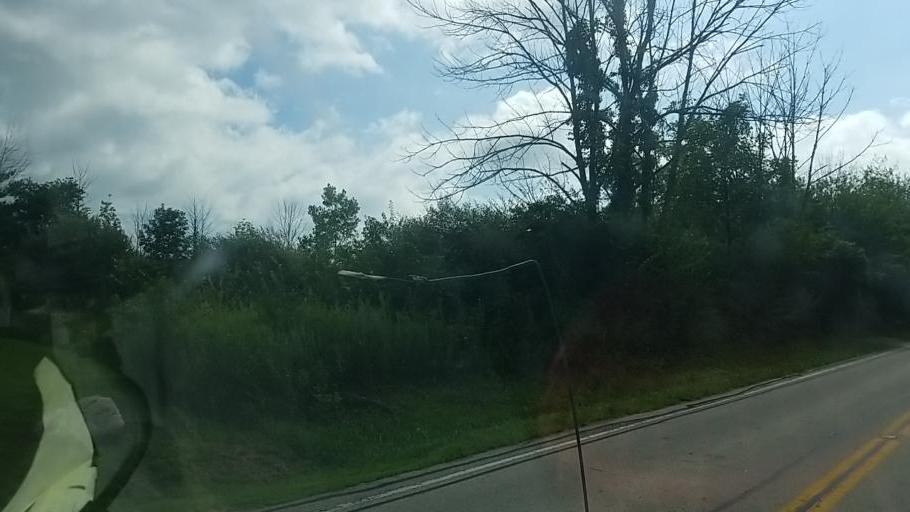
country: US
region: Ohio
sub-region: Pickaway County
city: Commercial Point
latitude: 39.7912
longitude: -83.1694
